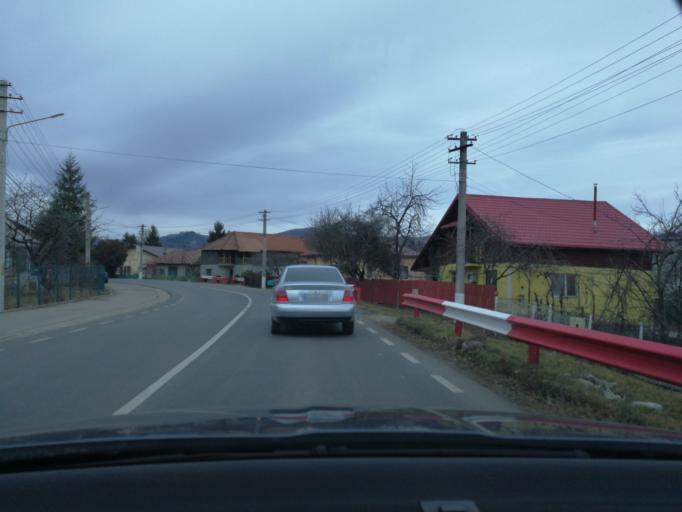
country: RO
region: Prahova
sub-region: Comuna Cornu
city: Cornu de Jos
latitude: 45.1476
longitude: 25.6918
